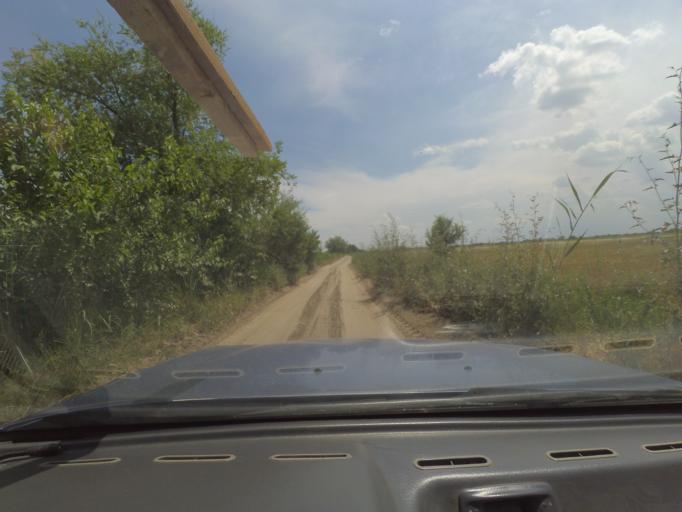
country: TJ
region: Viloyati Sughd
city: Buston
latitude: 40.5526
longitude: 69.0753
